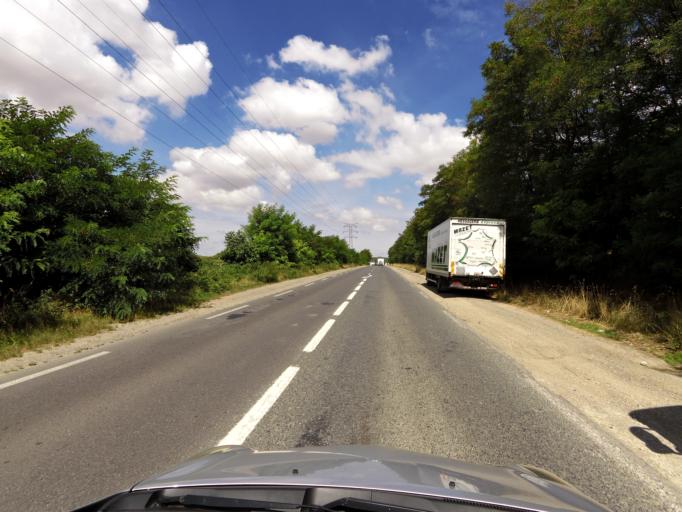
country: FR
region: Ile-de-France
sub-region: Departement de Seine-et-Marne
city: Chauconin-Neufmontiers
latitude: 48.9655
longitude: 2.8597
